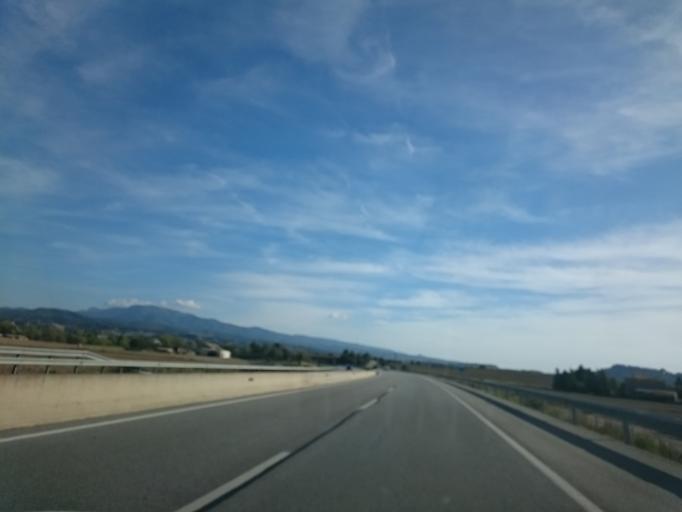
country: ES
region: Catalonia
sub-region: Provincia de Barcelona
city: Vic
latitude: 41.9189
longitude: 2.2370
